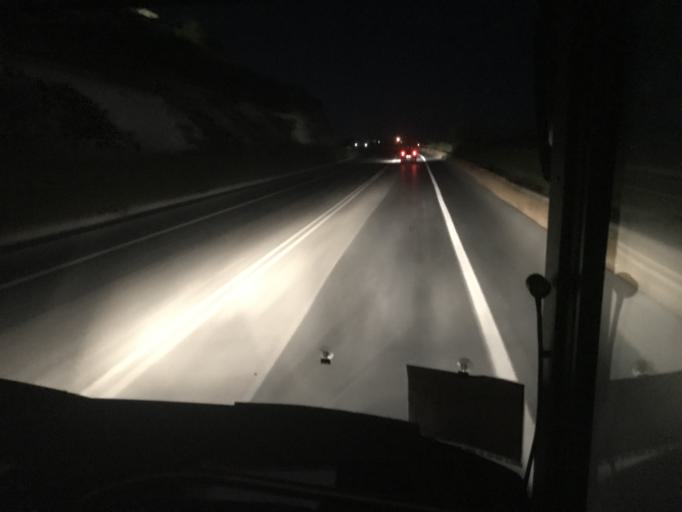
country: GR
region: Crete
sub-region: Nomos Irakleiou
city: Skalanion
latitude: 35.2591
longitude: 25.1810
